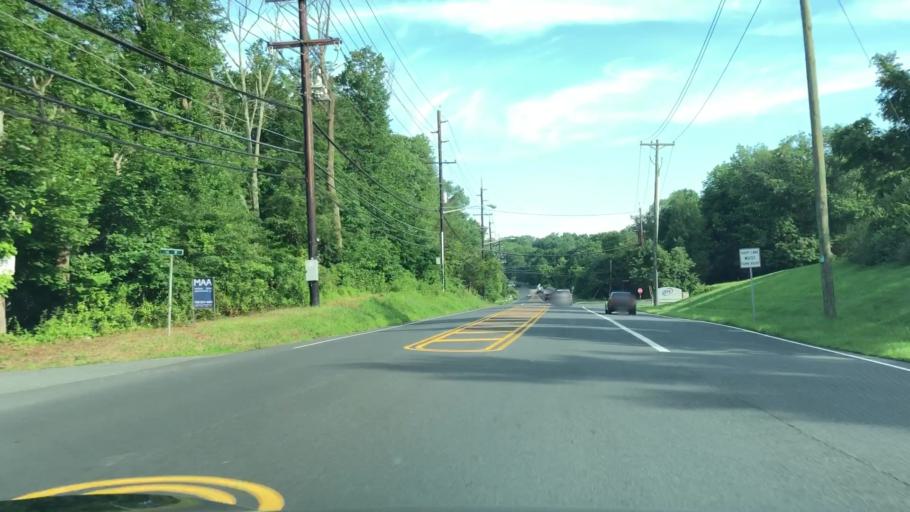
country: US
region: New Jersey
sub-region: Mercer County
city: Lawrenceville
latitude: 40.3407
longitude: -74.7236
